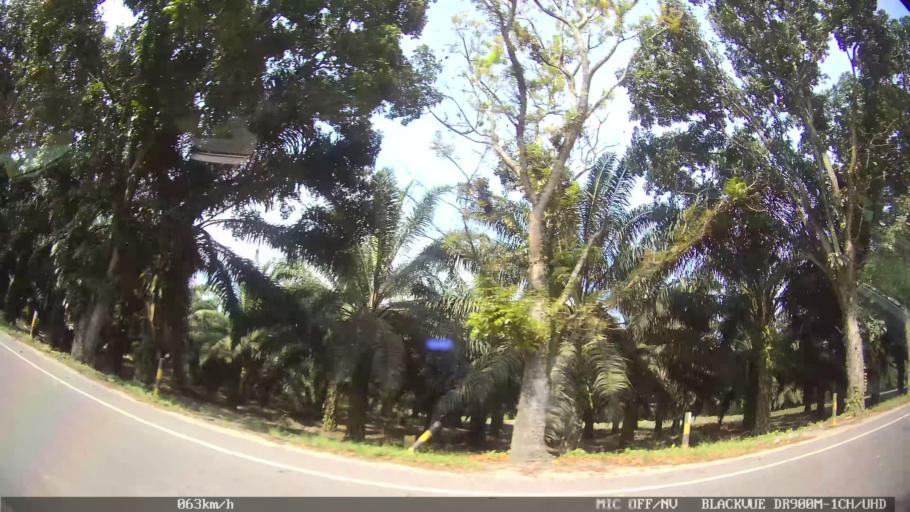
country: ID
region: North Sumatra
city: Binjai
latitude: 3.6514
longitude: 98.5337
